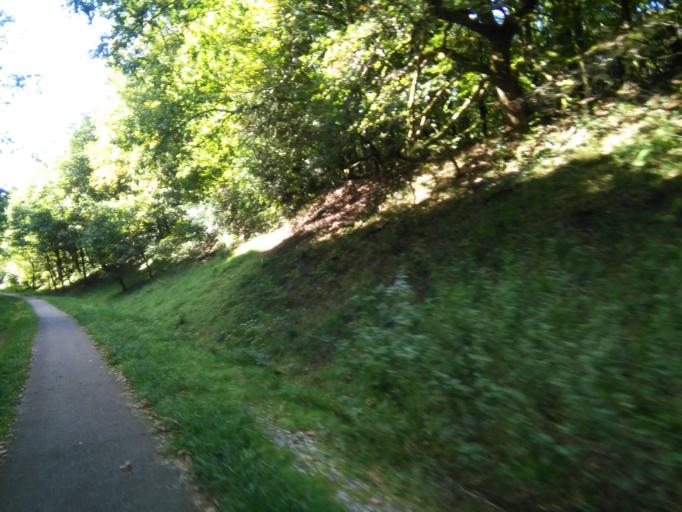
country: DK
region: Central Jutland
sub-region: Silkeborg Kommune
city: Silkeborg
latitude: 56.1307
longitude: 9.4241
